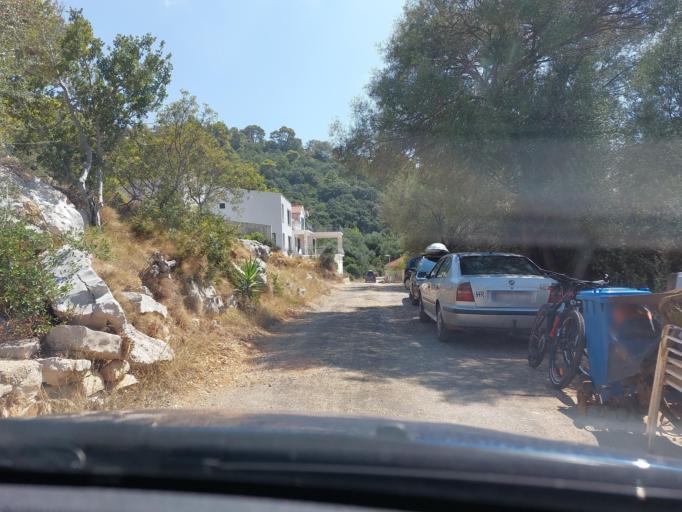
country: HR
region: Dubrovacko-Neretvanska
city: Smokvica
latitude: 42.7727
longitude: 16.8388
